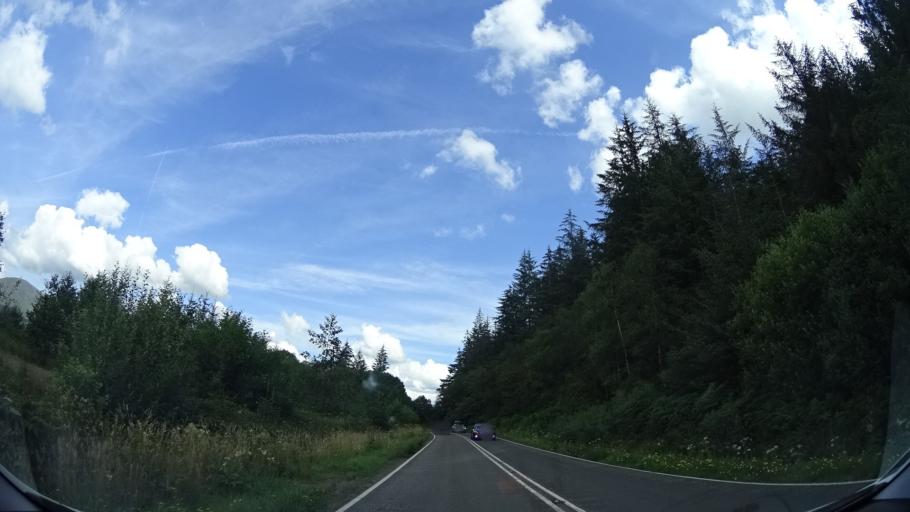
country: GB
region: Scotland
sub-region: Highland
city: Fort William
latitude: 56.7478
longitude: -5.1983
